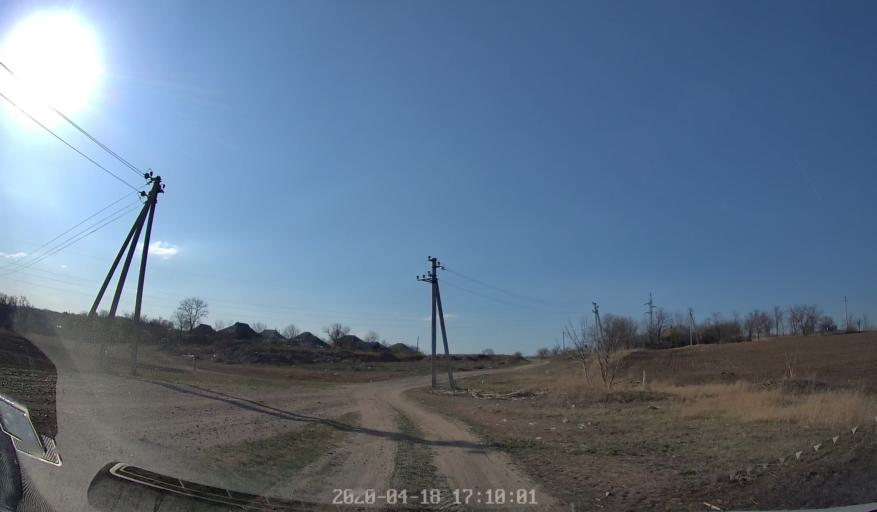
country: MD
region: Chisinau
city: Vadul lui Voda
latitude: 47.1483
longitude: 29.0859
